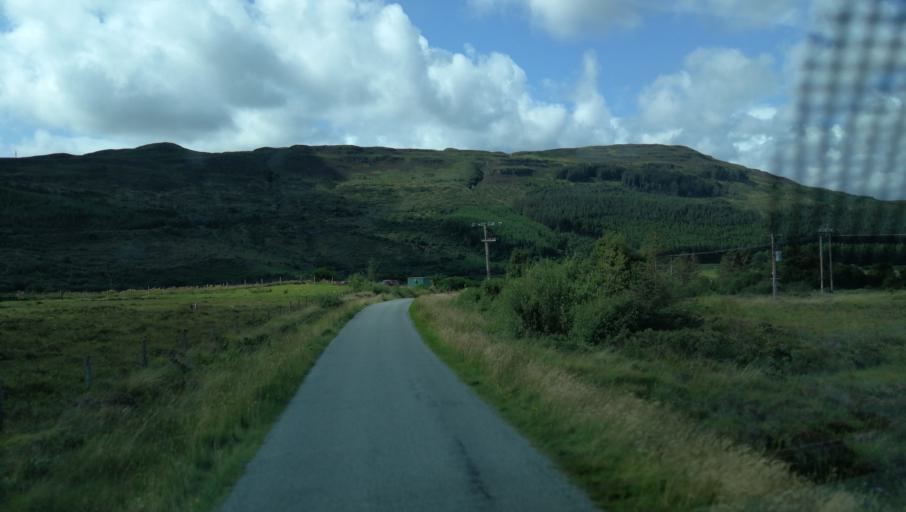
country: GB
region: Scotland
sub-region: Highland
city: Portree
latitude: 57.3853
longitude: -6.1933
